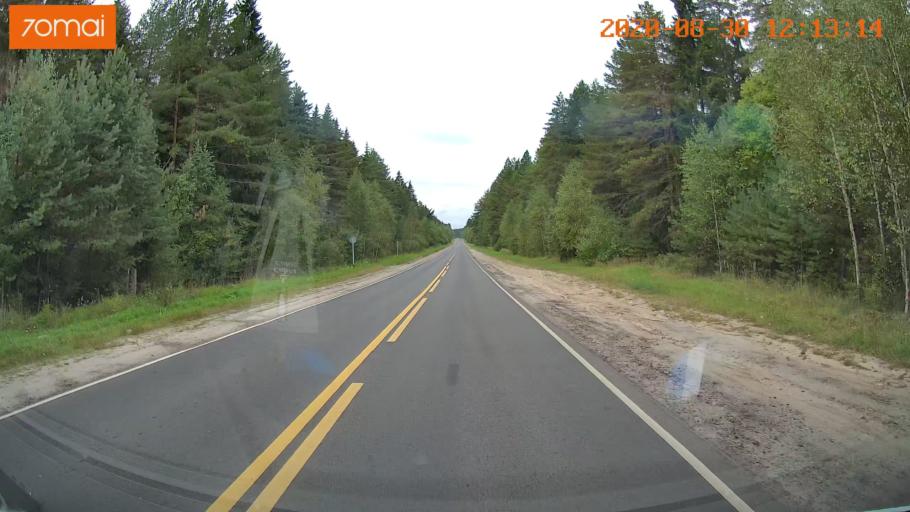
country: RU
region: Ivanovo
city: Yur'yevets
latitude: 57.3125
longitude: 43.0827
